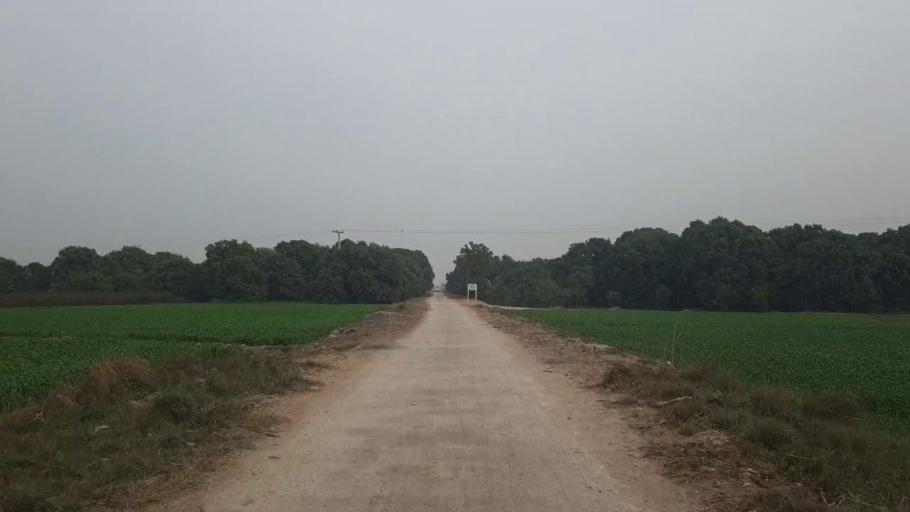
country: PK
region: Sindh
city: Tando Adam
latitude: 25.8452
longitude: 68.6608
